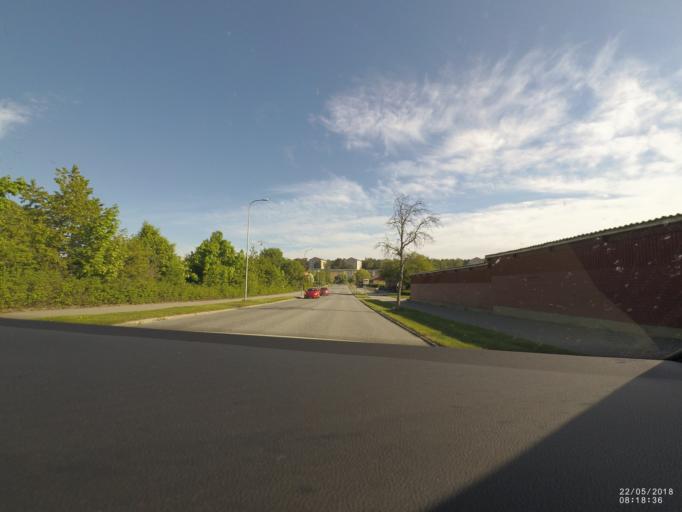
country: SE
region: Soedermanland
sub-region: Nykopings Kommun
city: Nykoping
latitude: 58.7520
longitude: 17.0435
